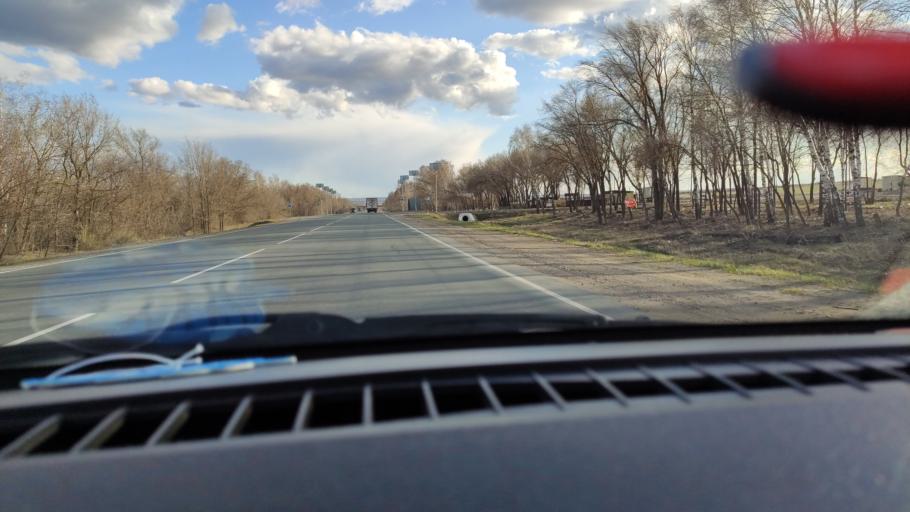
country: RU
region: Saratov
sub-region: Saratovskiy Rayon
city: Saratov
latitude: 51.7016
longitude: 46.0115
